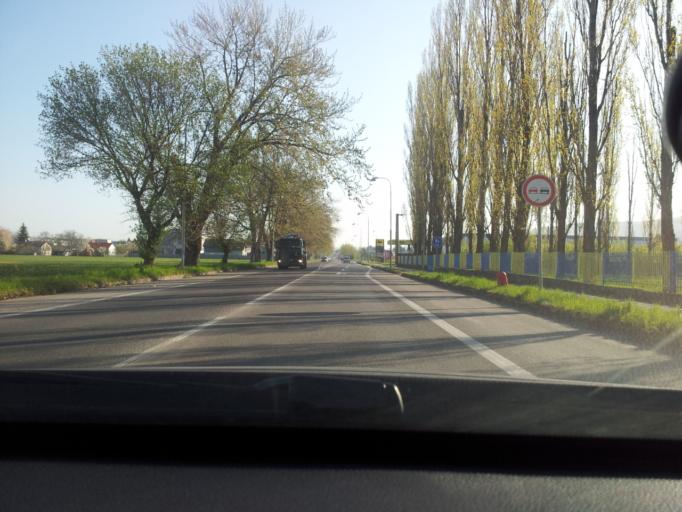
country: SK
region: Nitriansky
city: Zlate Moravce
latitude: 48.3910
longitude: 18.3949
